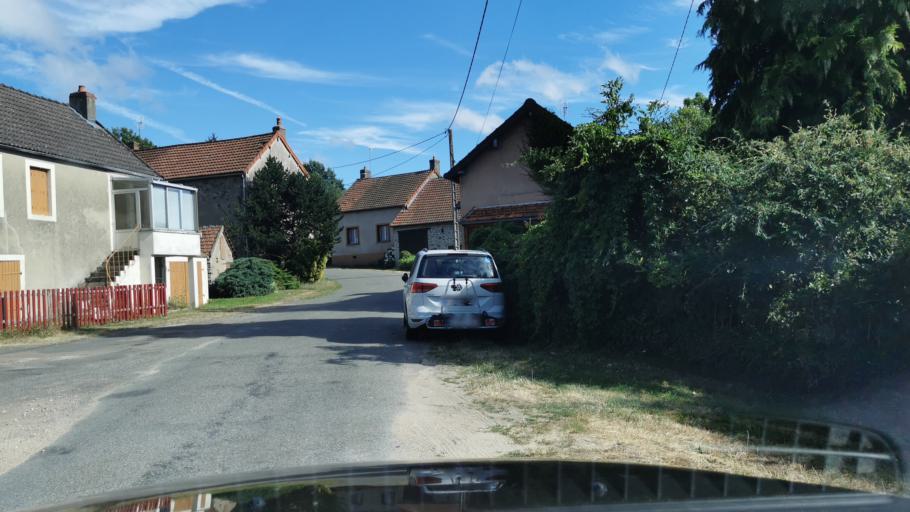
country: FR
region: Bourgogne
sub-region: Departement de Saone-et-Loire
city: Marmagne
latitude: 46.8729
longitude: 4.3421
